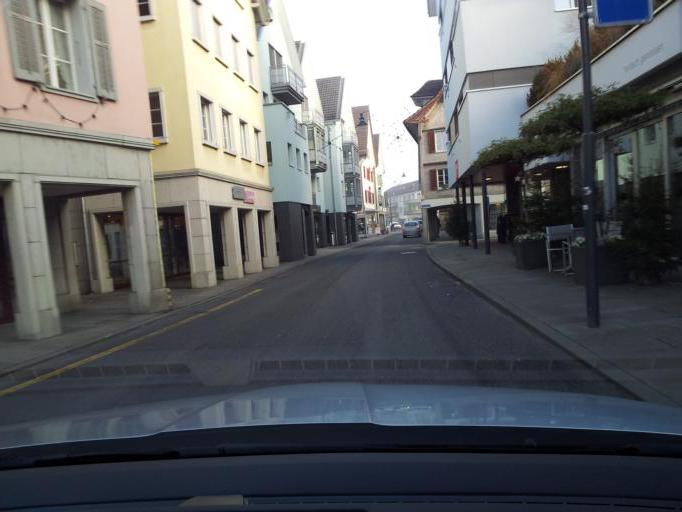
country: CH
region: Obwalden
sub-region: Obwalden
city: Sarnen
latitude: 46.8960
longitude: 8.2456
